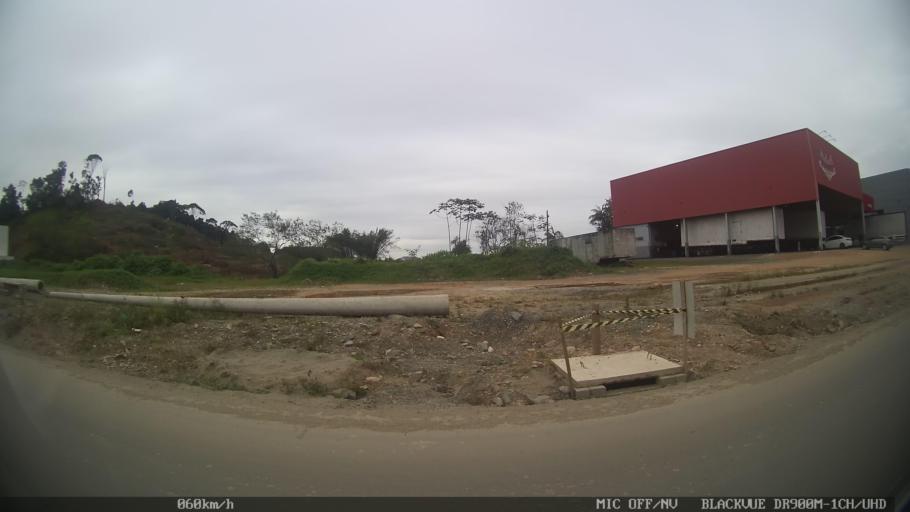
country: BR
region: Santa Catarina
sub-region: Joinville
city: Joinville
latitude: -26.2521
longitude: -48.8681
